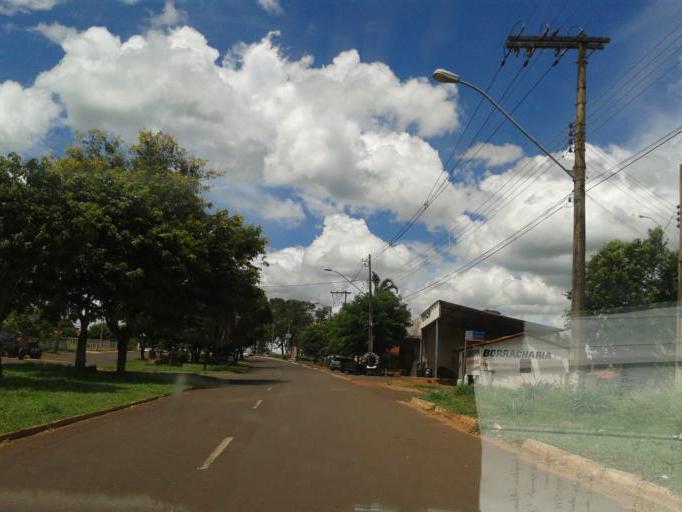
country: BR
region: Minas Gerais
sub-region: Santa Vitoria
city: Santa Vitoria
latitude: -18.8470
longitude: -50.1312
